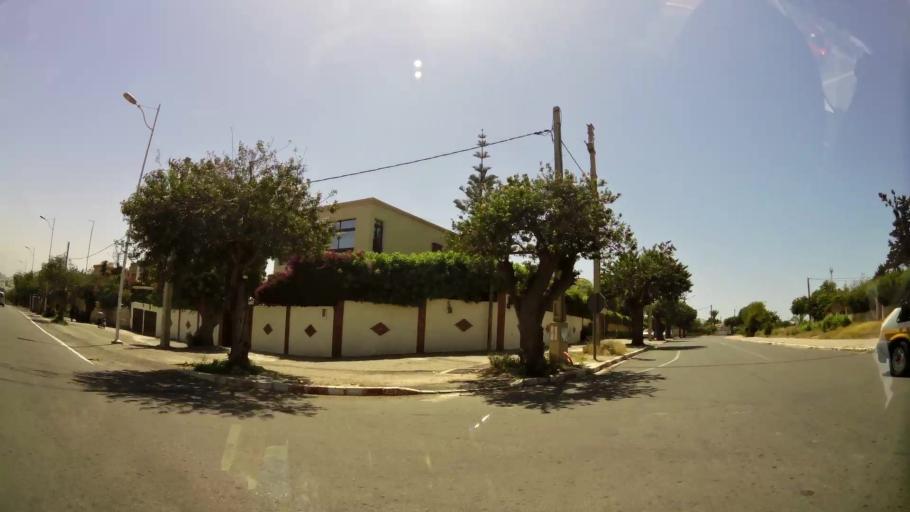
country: MA
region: Souss-Massa-Draa
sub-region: Agadir-Ida-ou-Tnan
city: Agadir
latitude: 30.4317
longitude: -9.5940
